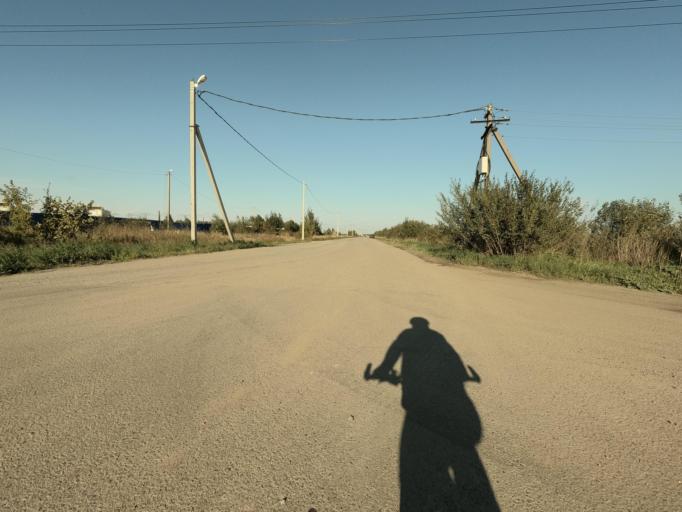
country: RU
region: St.-Petersburg
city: Petro-Slavyanka
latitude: 59.7647
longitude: 30.4854
